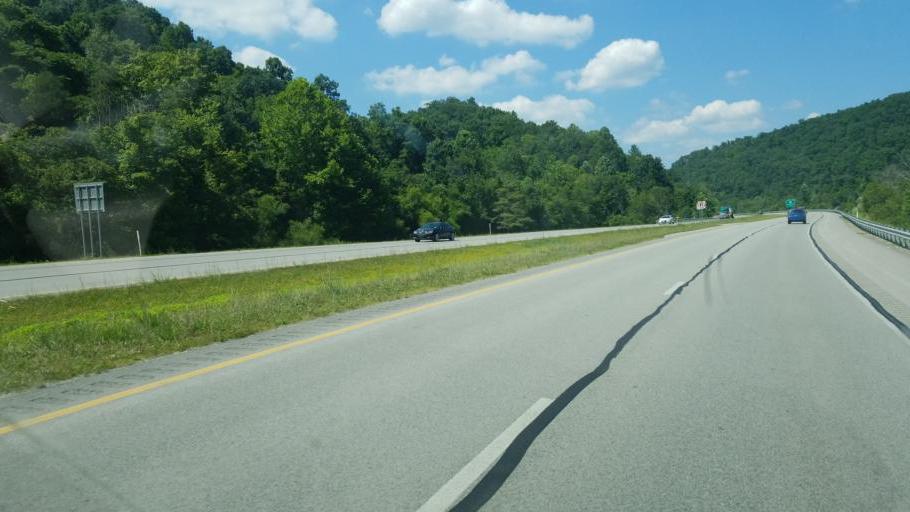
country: US
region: West Virginia
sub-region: Kanawha County
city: Sissonville
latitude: 38.5787
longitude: -81.6410
